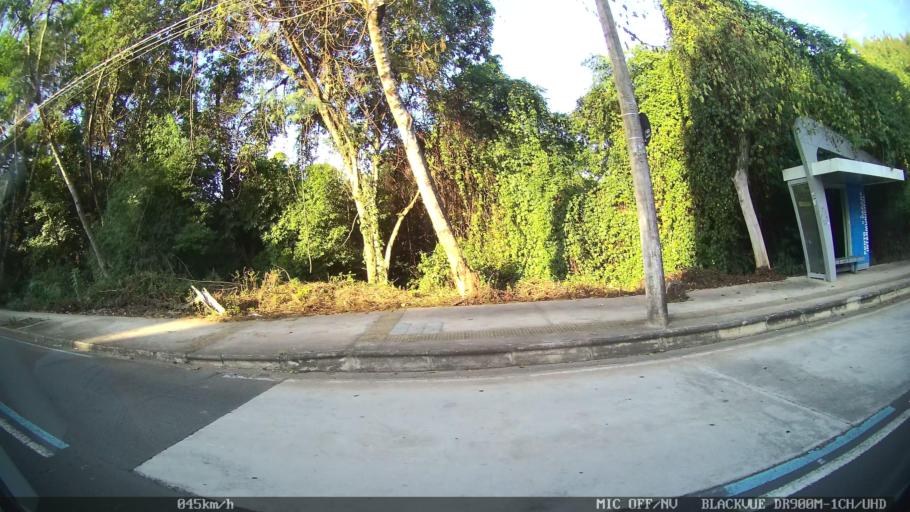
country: BR
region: Sao Paulo
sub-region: Piracicaba
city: Piracicaba
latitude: -22.7128
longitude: -47.6525
